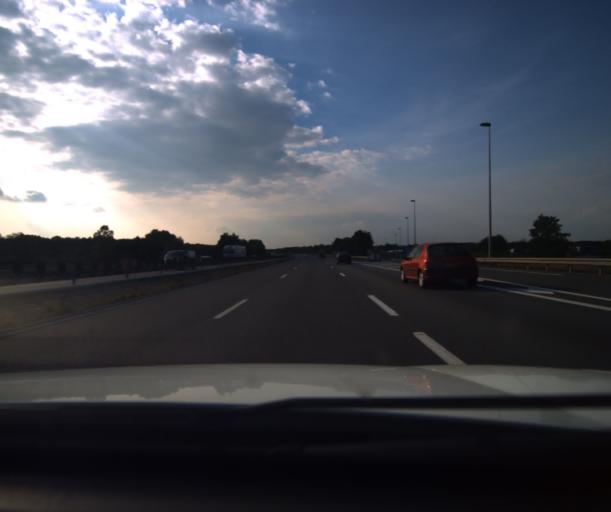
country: FR
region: Midi-Pyrenees
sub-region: Departement de la Haute-Garonne
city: Castelnau-d'Estretefonds
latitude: 43.8094
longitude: 1.3639
